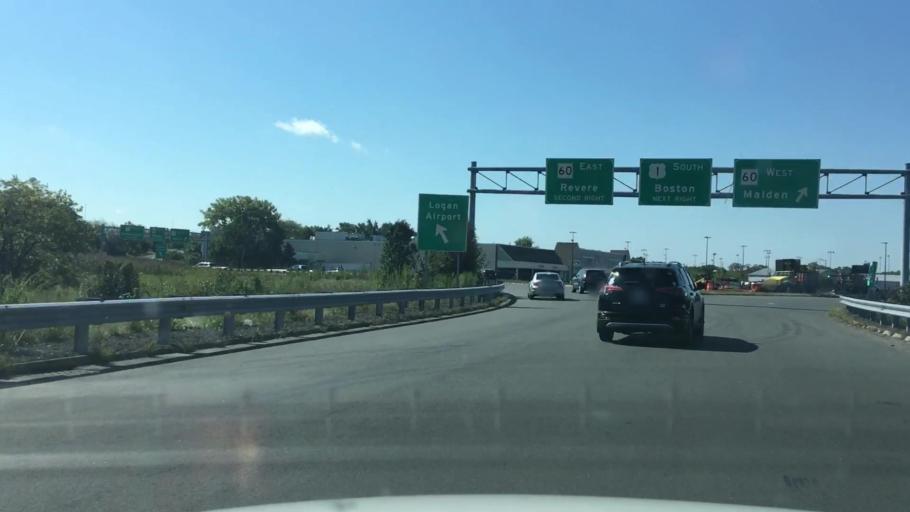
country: US
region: Massachusetts
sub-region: Suffolk County
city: Revere
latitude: 42.4309
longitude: -71.0185
